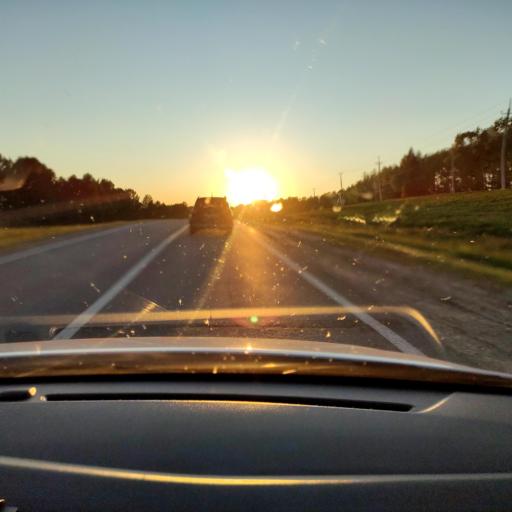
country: RU
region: Tatarstan
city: Pestretsy
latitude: 55.8199
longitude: 49.5365
